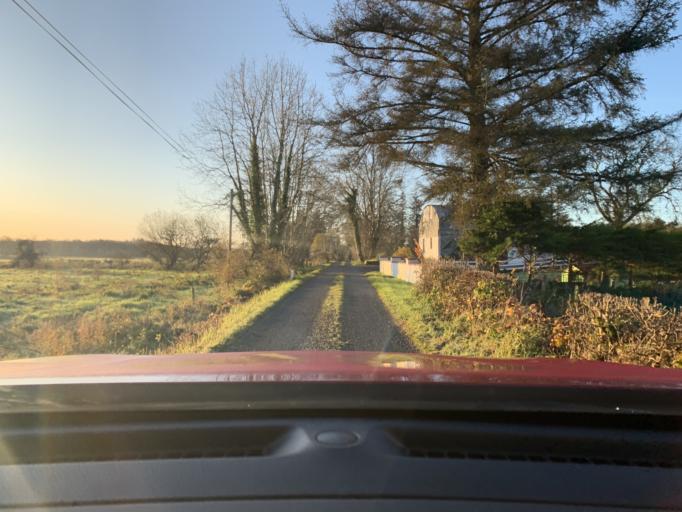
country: IE
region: Connaught
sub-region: Sligo
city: Ballymote
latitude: 54.0816
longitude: -8.5468
